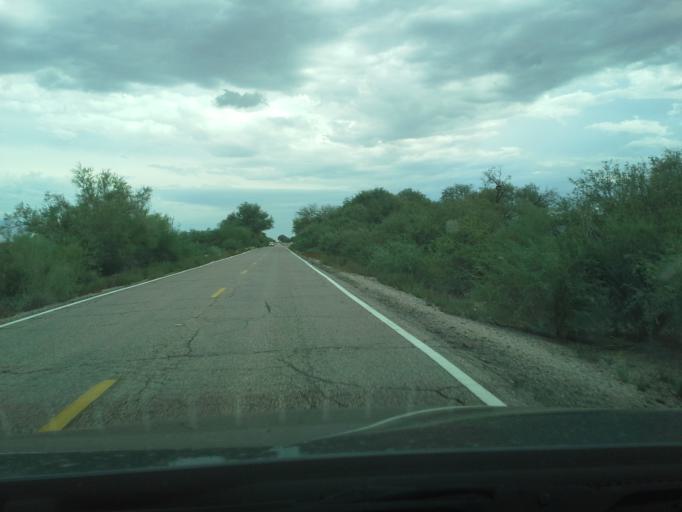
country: US
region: Arizona
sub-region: Pima County
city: Marana
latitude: 32.4689
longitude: -111.2250
